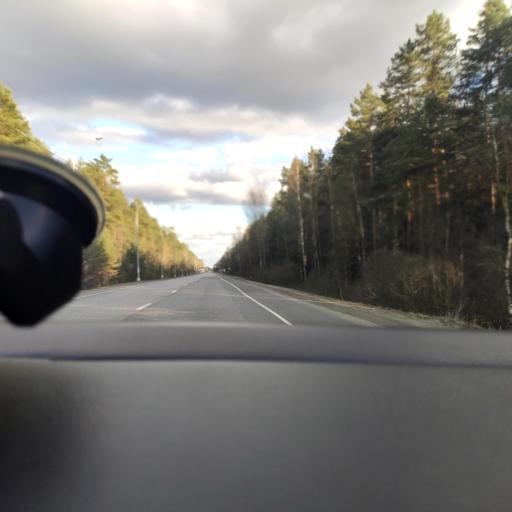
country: RU
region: Moskovskaya
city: Il'inskiy Pogost
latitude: 55.4623
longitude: 38.9796
